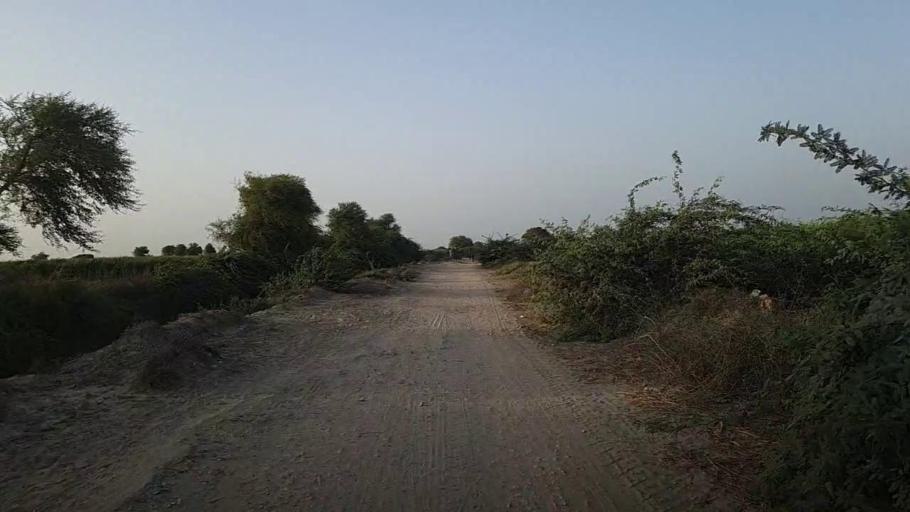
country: PK
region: Sindh
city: Kario
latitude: 24.7062
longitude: 68.4649
